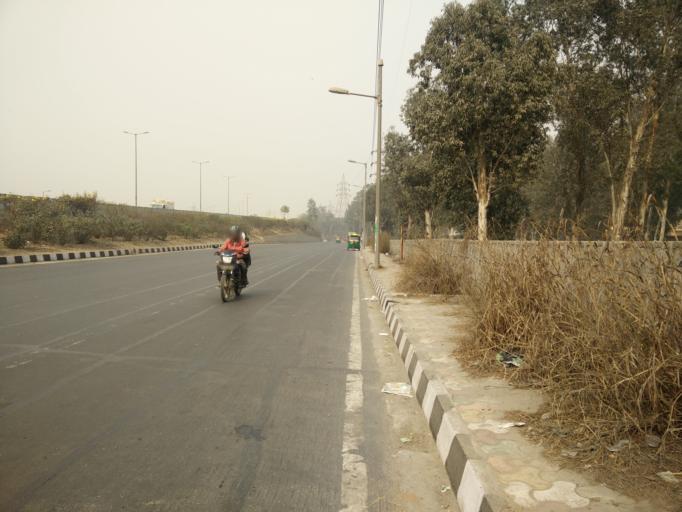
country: IN
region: Uttar Pradesh
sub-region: Gautam Buddha Nagar
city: Noida
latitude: 28.6503
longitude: 77.3193
